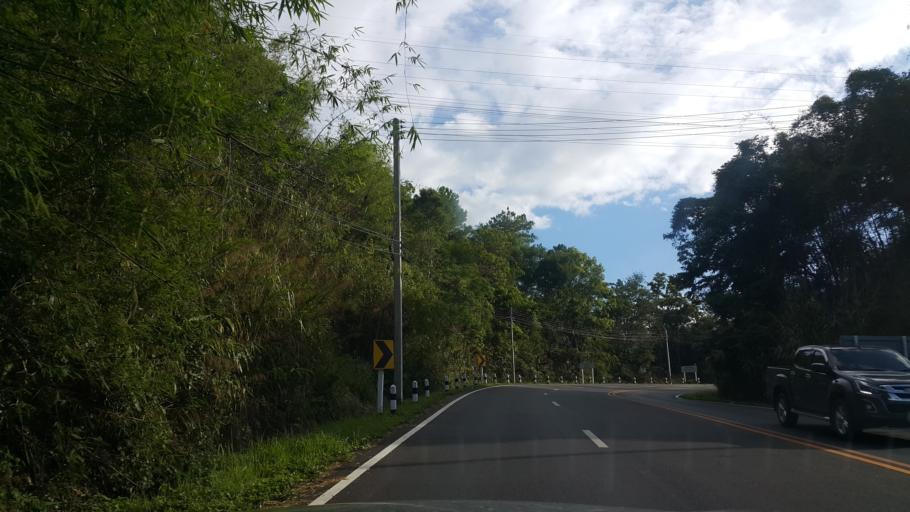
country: TH
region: Phayao
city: Phayao
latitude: 19.0609
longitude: 99.7809
